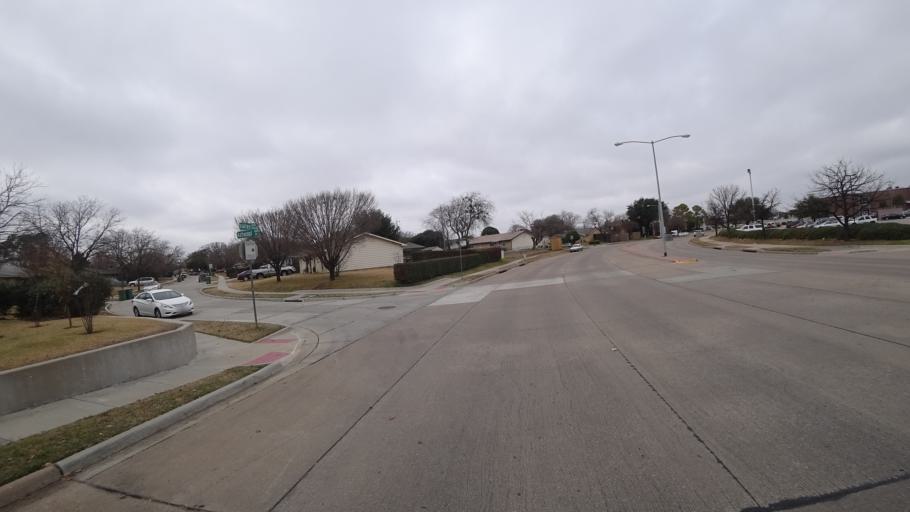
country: US
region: Texas
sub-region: Denton County
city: Lewisville
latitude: 33.0380
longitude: -97.0203
